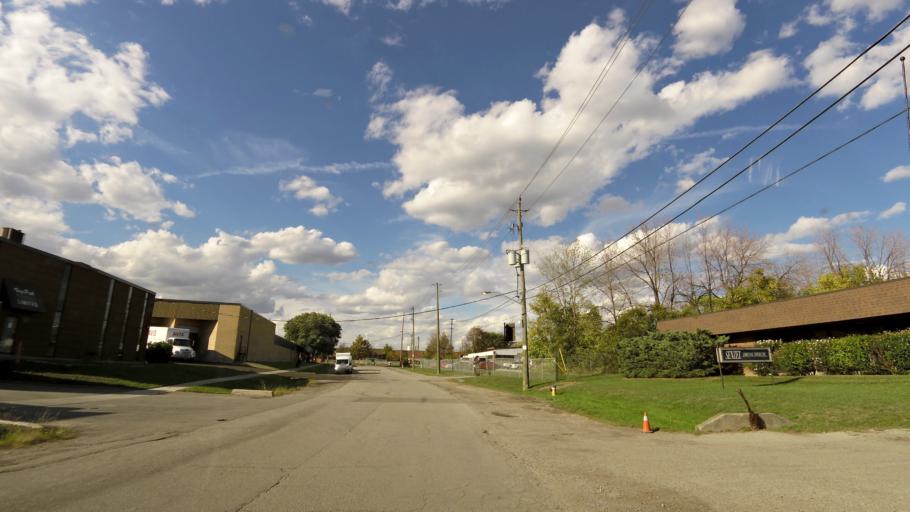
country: CA
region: Ontario
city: Etobicoke
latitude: 43.6045
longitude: -79.5261
